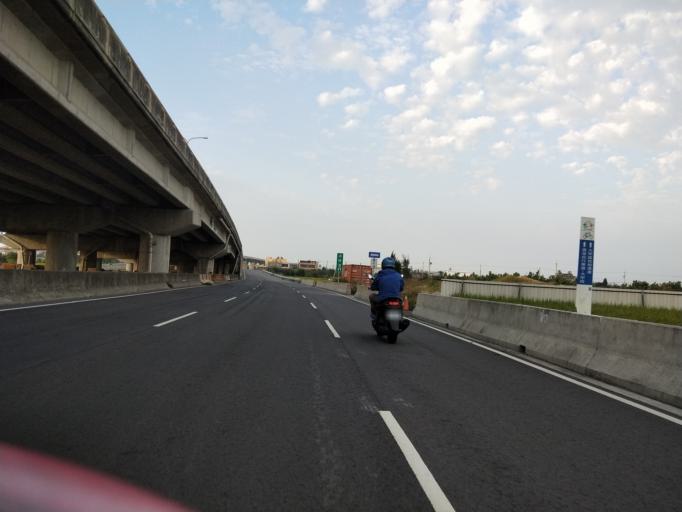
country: TW
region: Taiwan
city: Fengyuan
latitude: 24.4073
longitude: 120.6148
